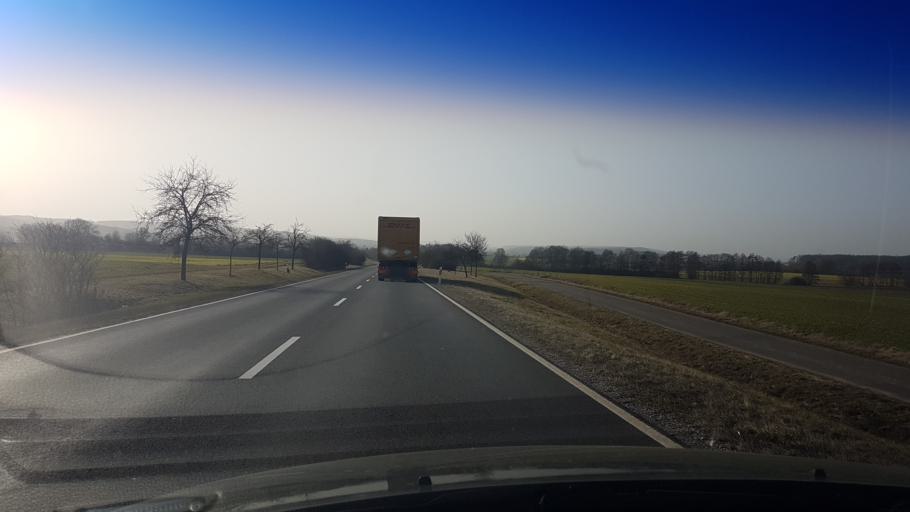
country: DE
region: Bavaria
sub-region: Upper Franconia
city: Walsdorf
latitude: 49.8331
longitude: 10.8048
